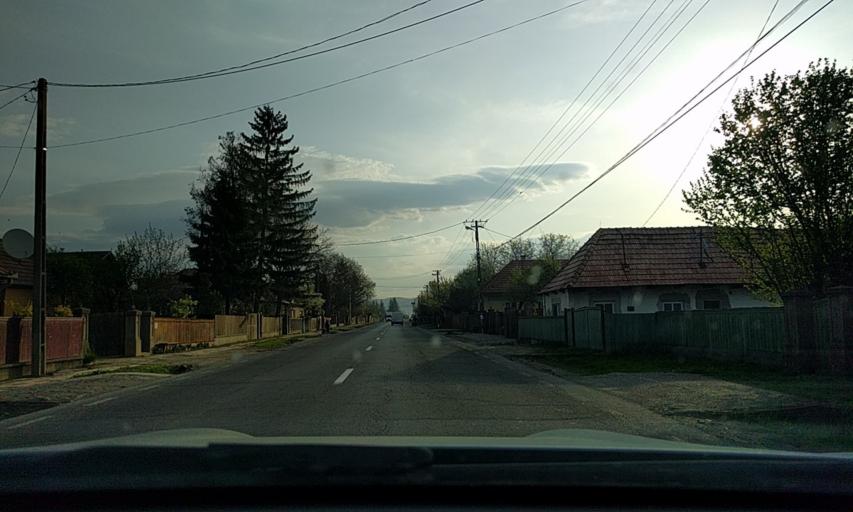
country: RO
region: Covasna
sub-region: Municipiul Targu Secuiesc
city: Lunga
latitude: 46.0277
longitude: 26.2286
